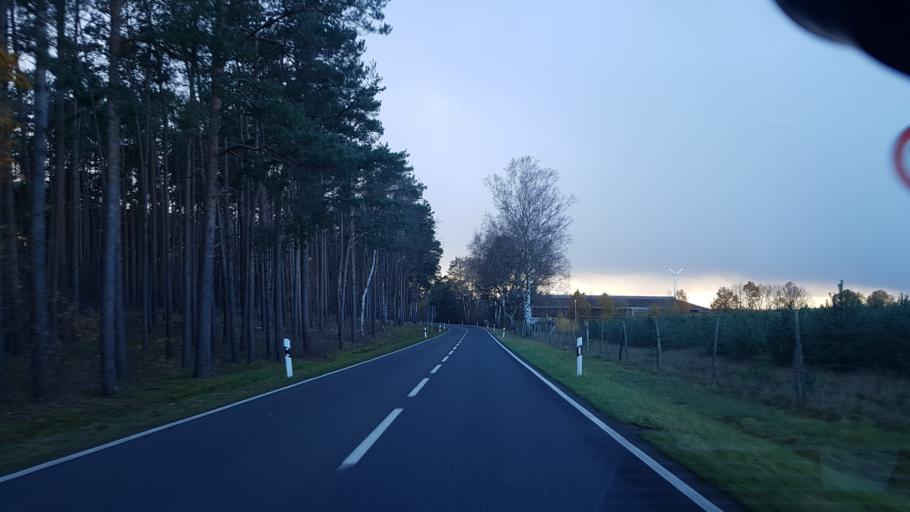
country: DE
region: Brandenburg
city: Sonnewalde
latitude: 51.7275
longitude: 13.6979
